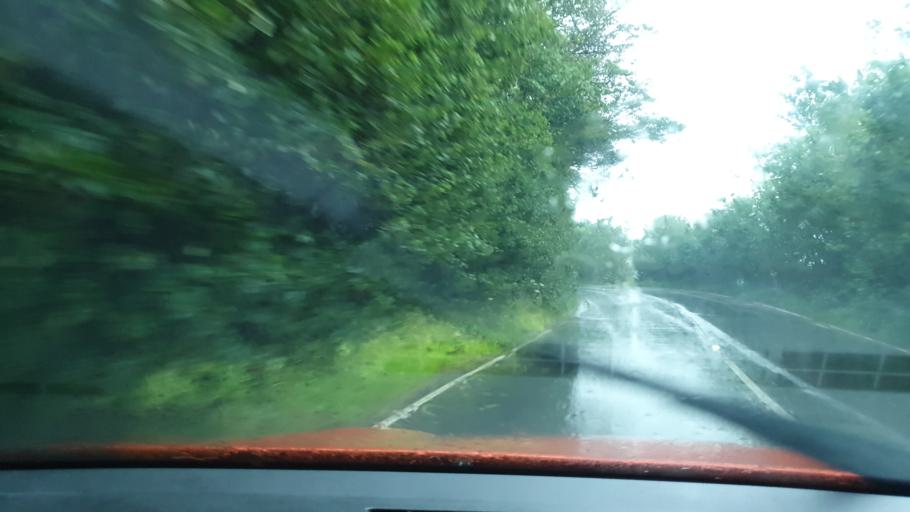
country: GB
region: England
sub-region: Cumbria
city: Askam in Furness
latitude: 54.2624
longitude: -3.1810
